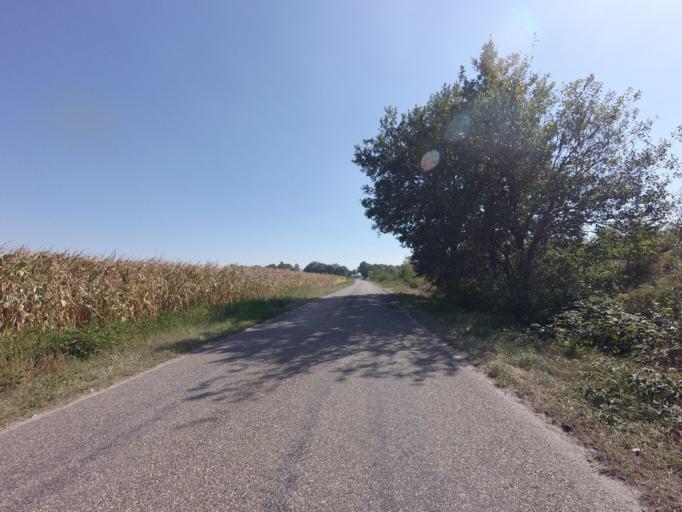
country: NL
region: North Brabant
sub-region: Gemeente Someren
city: Someren
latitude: 51.3801
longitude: 5.6719
